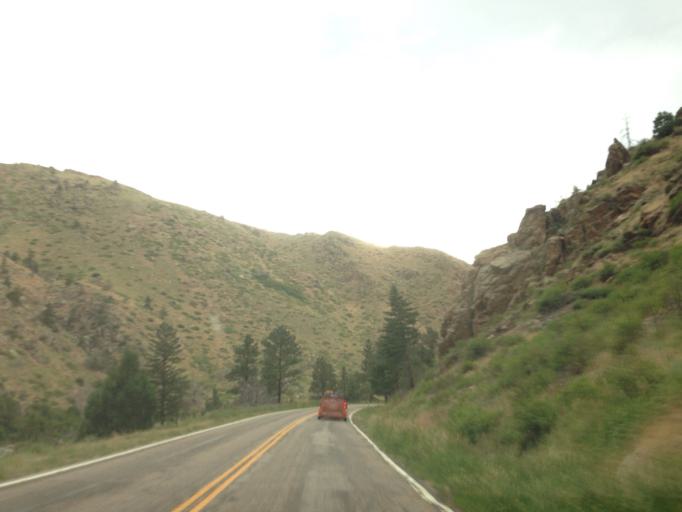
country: US
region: Colorado
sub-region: Larimer County
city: Laporte
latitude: 40.6804
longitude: -105.4111
